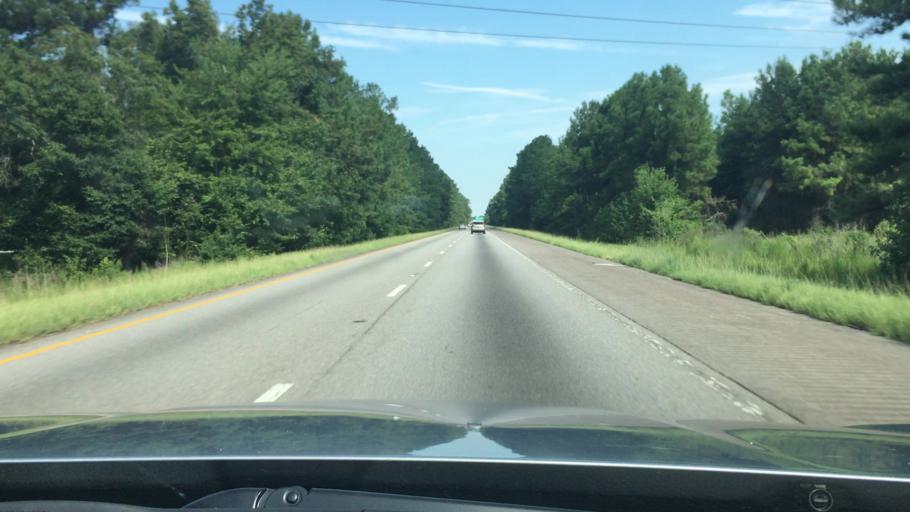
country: US
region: South Carolina
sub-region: Orangeburg County
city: Holly Hill
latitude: 33.3063
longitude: -80.5360
